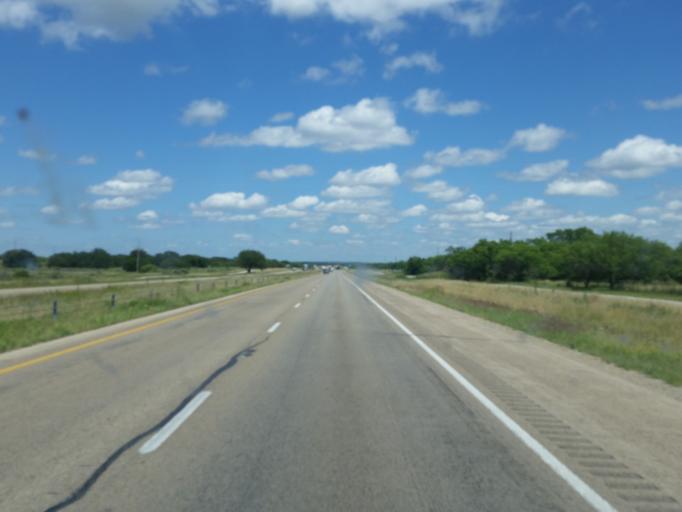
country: US
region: Texas
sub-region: Callahan County
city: Baird
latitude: 32.3891
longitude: -99.3257
